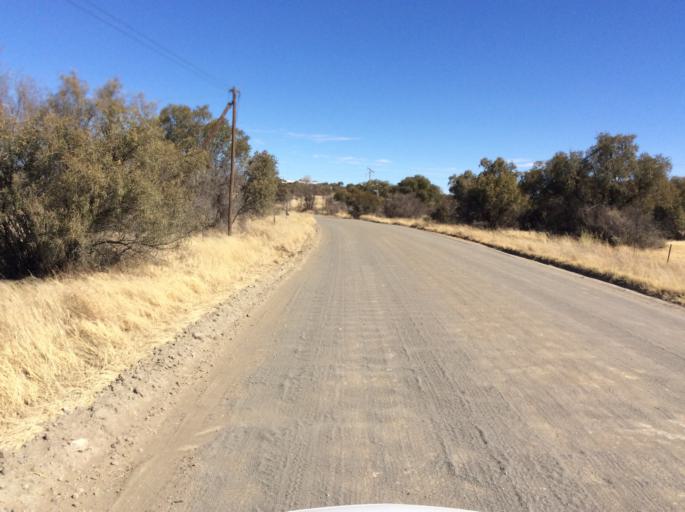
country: ZA
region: Orange Free State
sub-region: Lejweleputswa District Municipality
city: Brandfort
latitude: -28.7170
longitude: 26.0624
